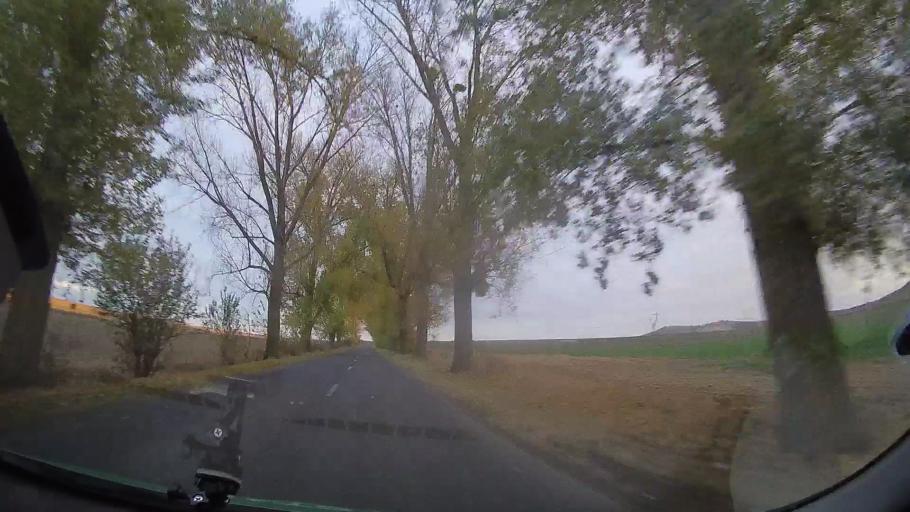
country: RO
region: Tulcea
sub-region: Comuna Nalbant
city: Nicolae Balcescu
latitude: 44.9889
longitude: 28.6069
